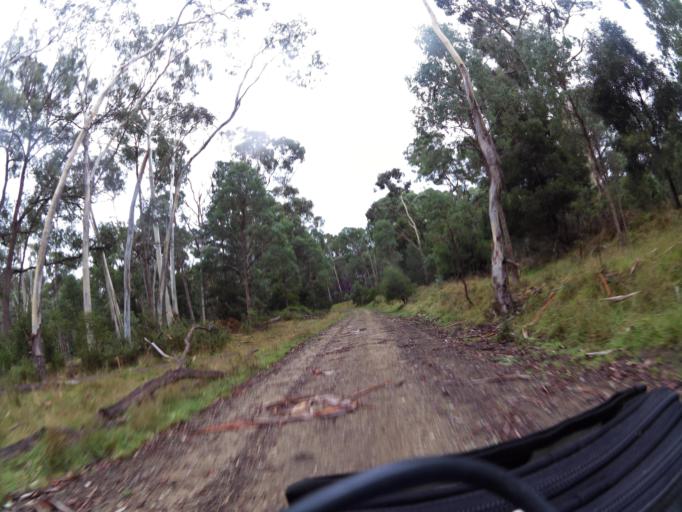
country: AU
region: New South Wales
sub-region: Greater Hume Shire
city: Holbrook
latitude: -36.1700
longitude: 147.4956
